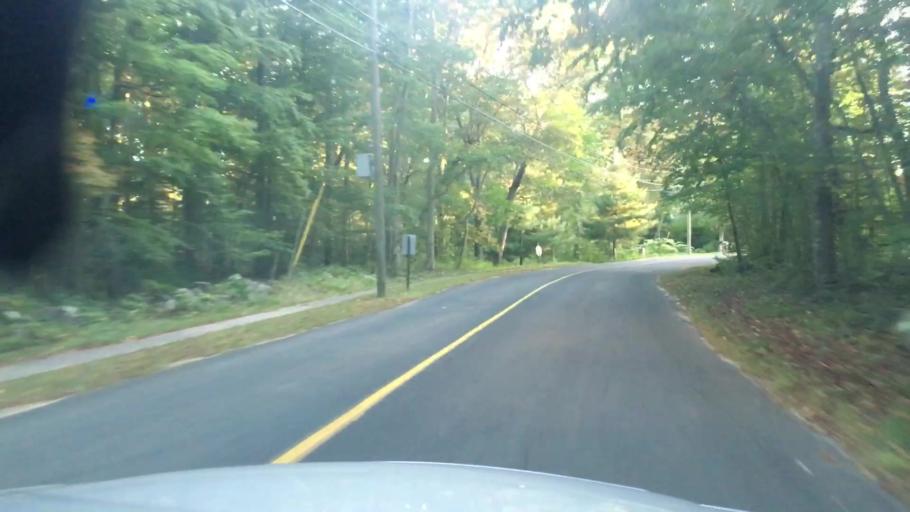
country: US
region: Connecticut
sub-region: Middlesex County
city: Westbrook Center
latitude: 41.3073
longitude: -72.4439
